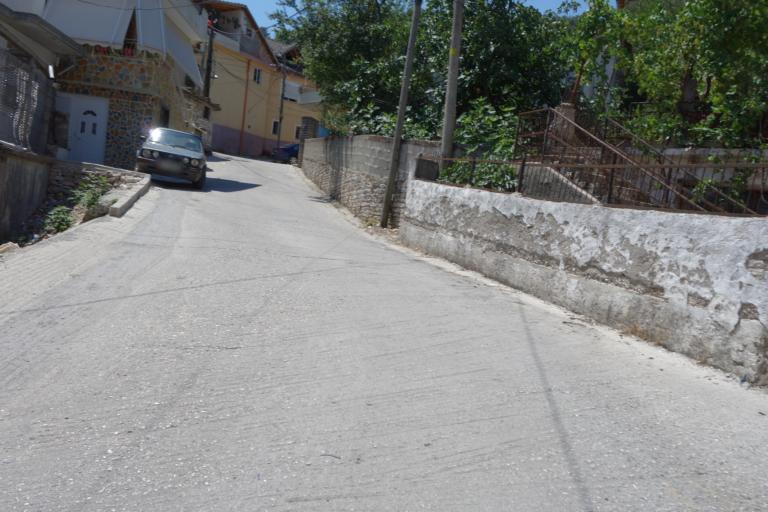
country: AL
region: Gjirokaster
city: Gjirokaster
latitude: 40.0788
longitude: 20.1344
